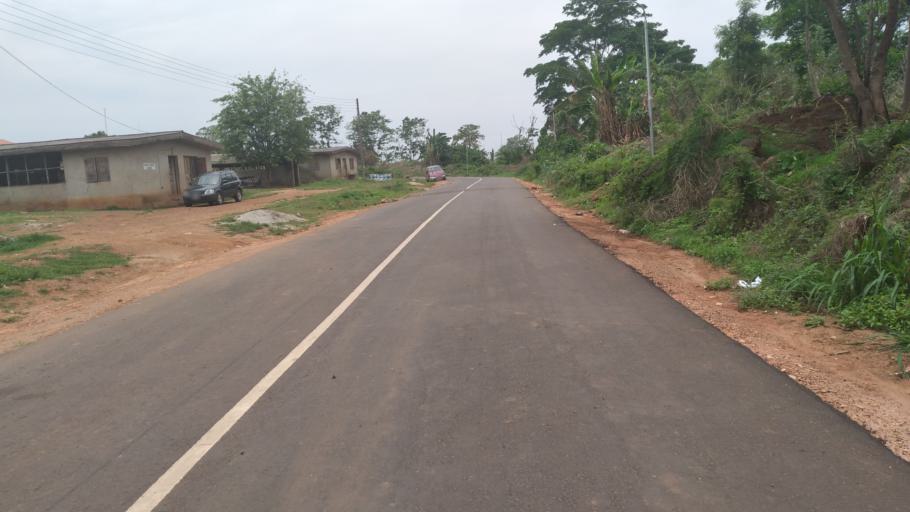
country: NG
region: Ondo
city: Ilare
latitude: 7.3001
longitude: 5.1449
